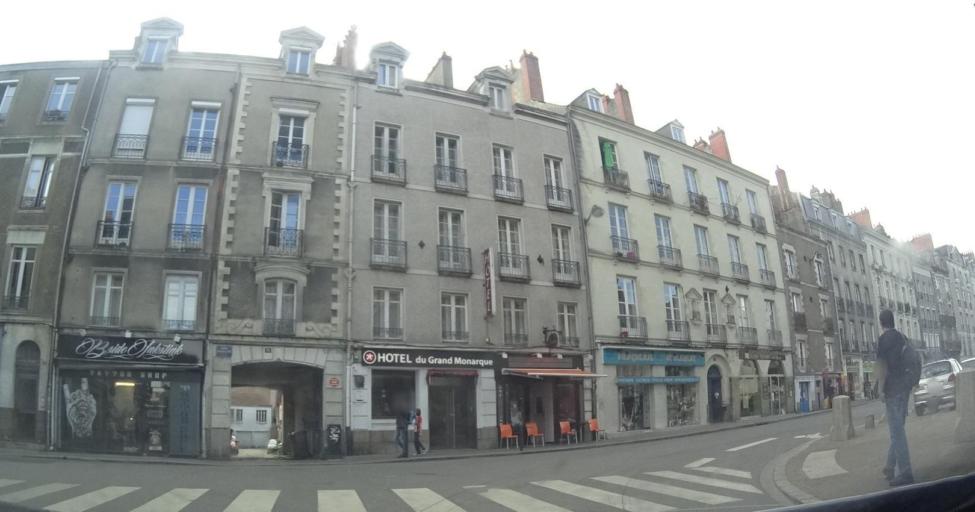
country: FR
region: Pays de la Loire
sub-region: Departement de la Loire-Atlantique
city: Nantes
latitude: 47.2215
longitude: -1.5475
